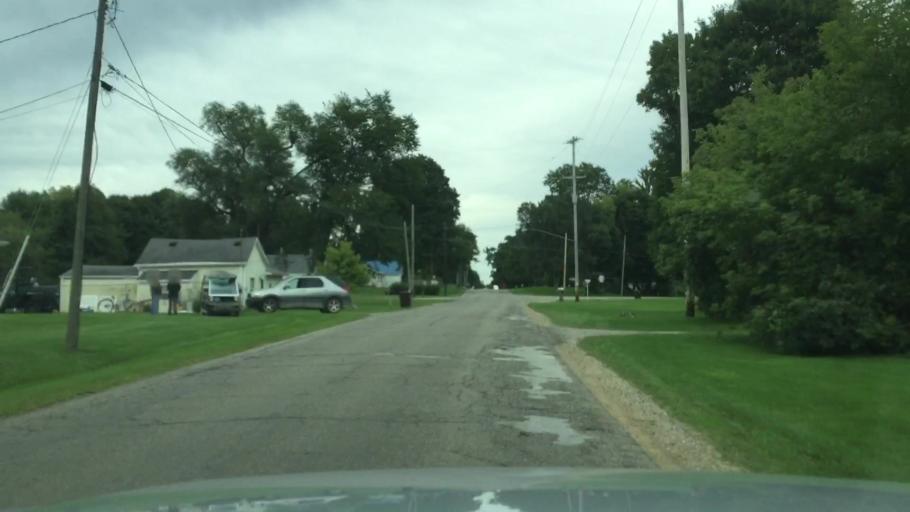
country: US
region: Michigan
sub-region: Shiawassee County
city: Durand
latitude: 42.8806
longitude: -84.0659
